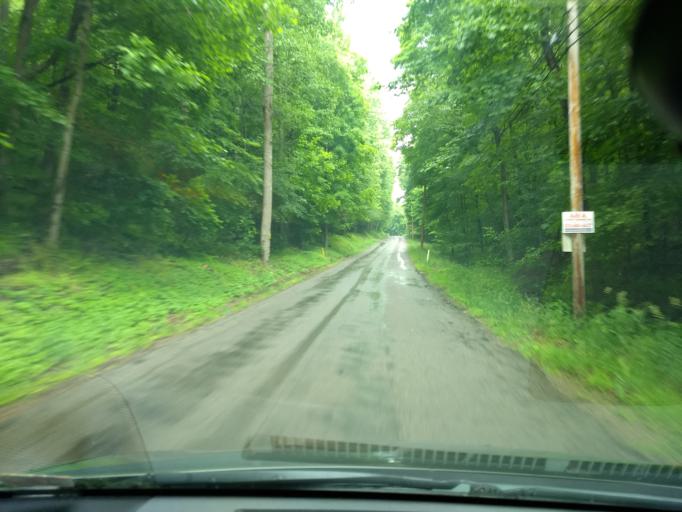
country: US
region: Pennsylvania
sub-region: Westmoreland County
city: Avonmore
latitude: 40.5296
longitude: -79.4916
